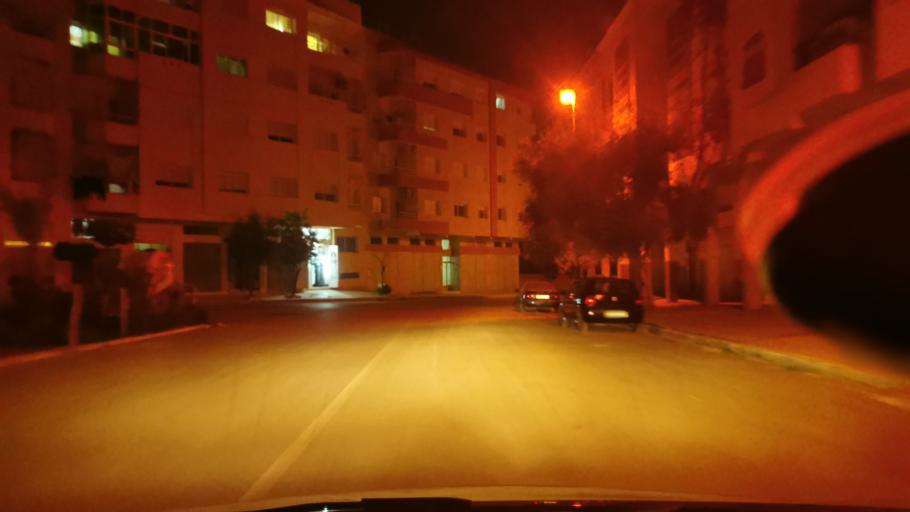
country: MA
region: Fes-Boulemane
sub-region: Fes
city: Fes
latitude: 34.0102
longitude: -4.9689
